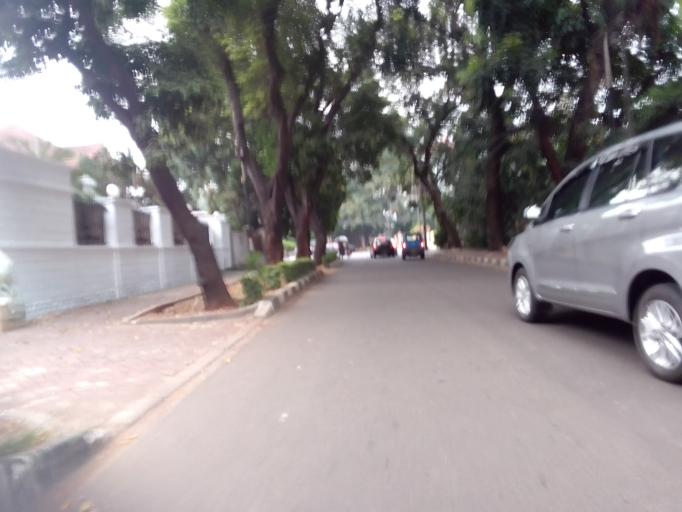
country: ID
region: Jakarta Raya
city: Jakarta
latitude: -6.2018
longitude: 106.8310
